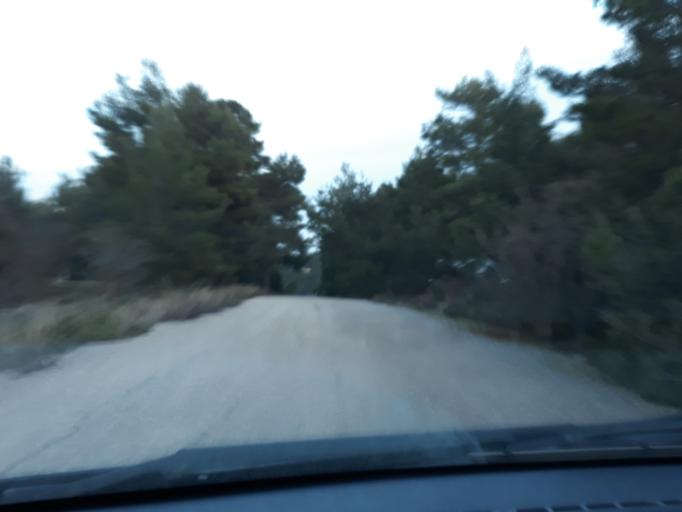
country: GR
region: Attica
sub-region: Nomarchia Anatolikis Attikis
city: Afidnes
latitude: 38.1934
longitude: 23.7986
